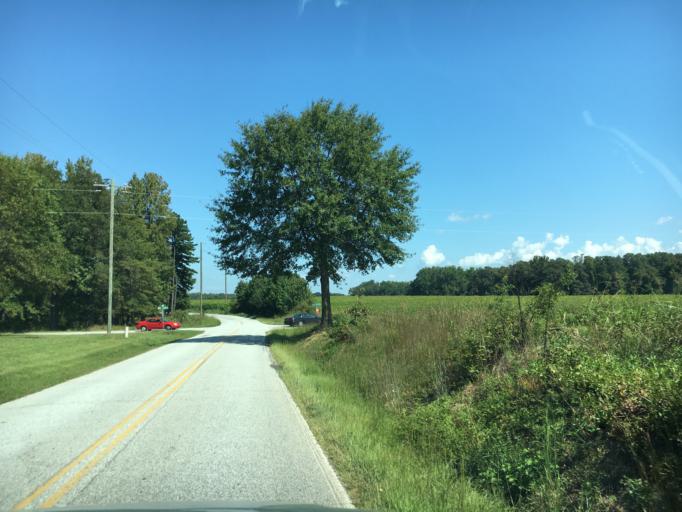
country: US
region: South Carolina
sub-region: Spartanburg County
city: Valley Falls
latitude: 35.0250
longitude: -81.9252
